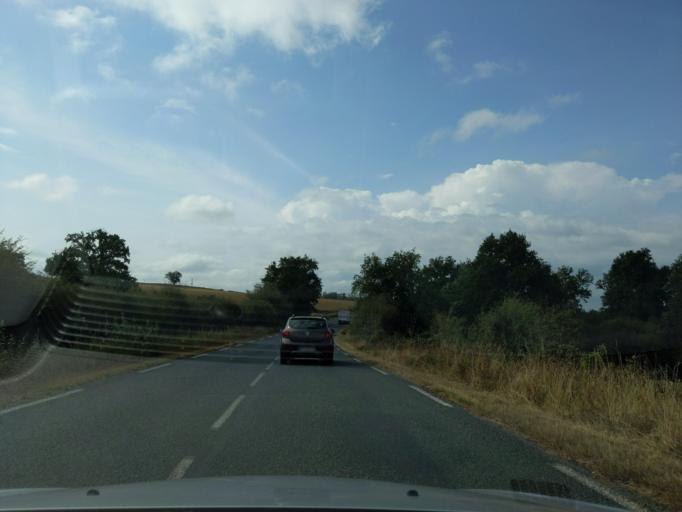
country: FR
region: Bourgogne
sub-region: Departement de Saone-et-Loire
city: Bourbon-Lancy
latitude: 46.6618
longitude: 3.7998
